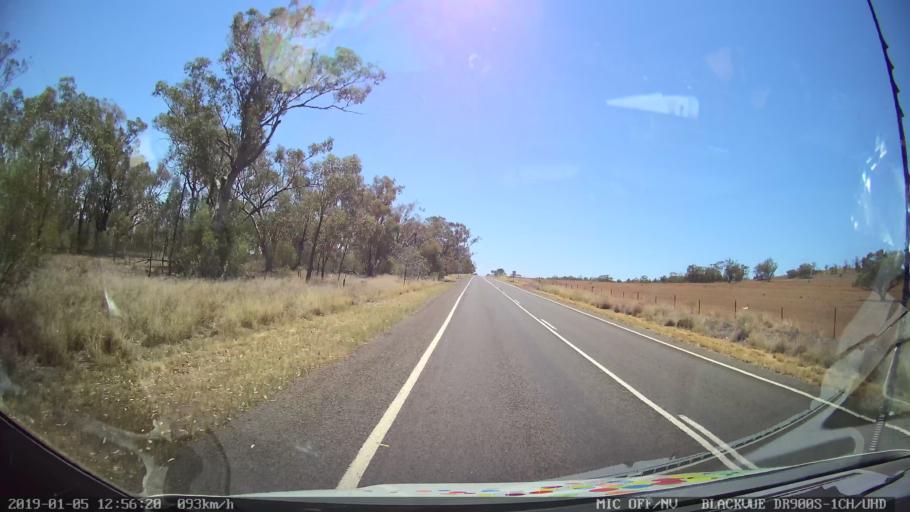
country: AU
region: New South Wales
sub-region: Warrumbungle Shire
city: Coonabarabran
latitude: -31.1152
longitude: 149.7188
